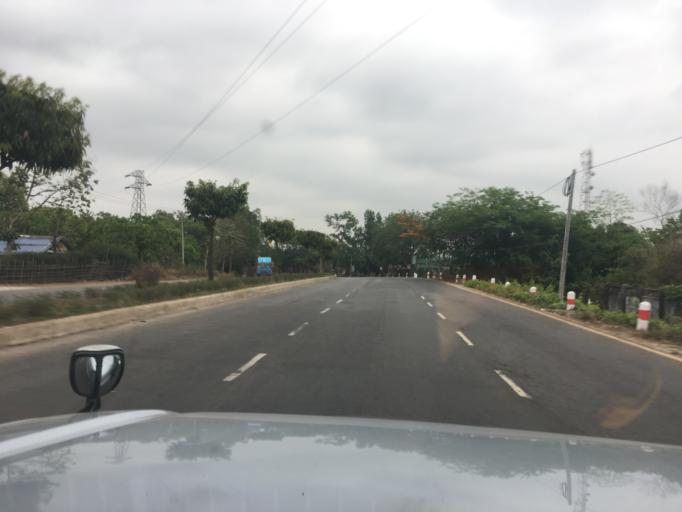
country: MM
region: Bago
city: Thanatpin
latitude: 17.2010
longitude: 96.4084
